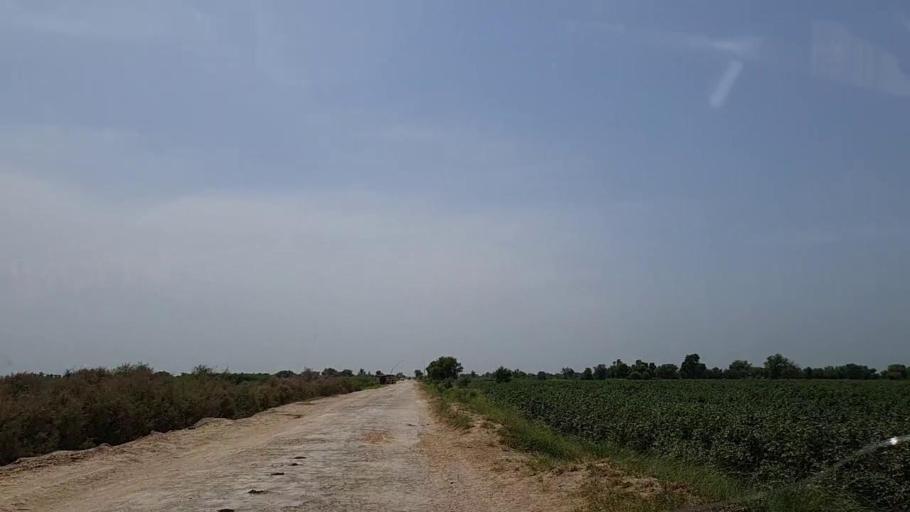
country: PK
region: Sindh
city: Khanpur
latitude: 27.8719
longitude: 69.4897
